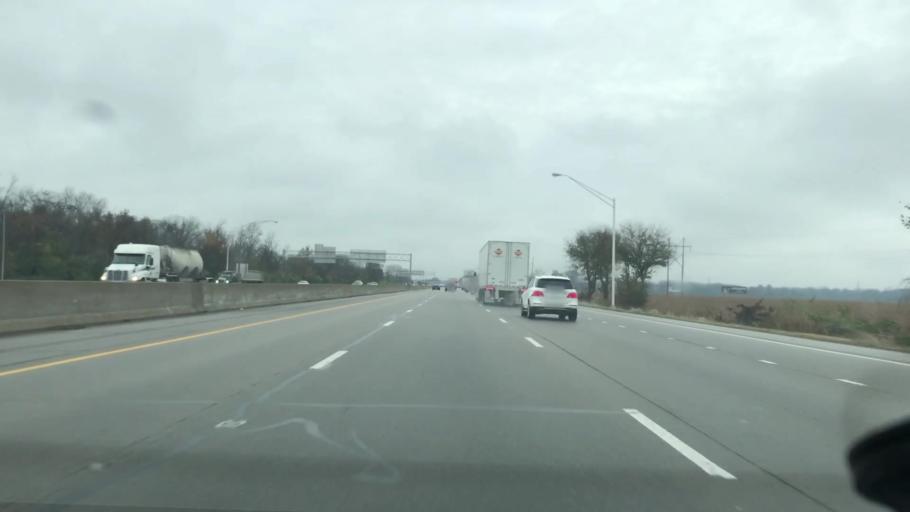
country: US
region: Ohio
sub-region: Clark County
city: Green Meadows
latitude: 39.8828
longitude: -83.9528
